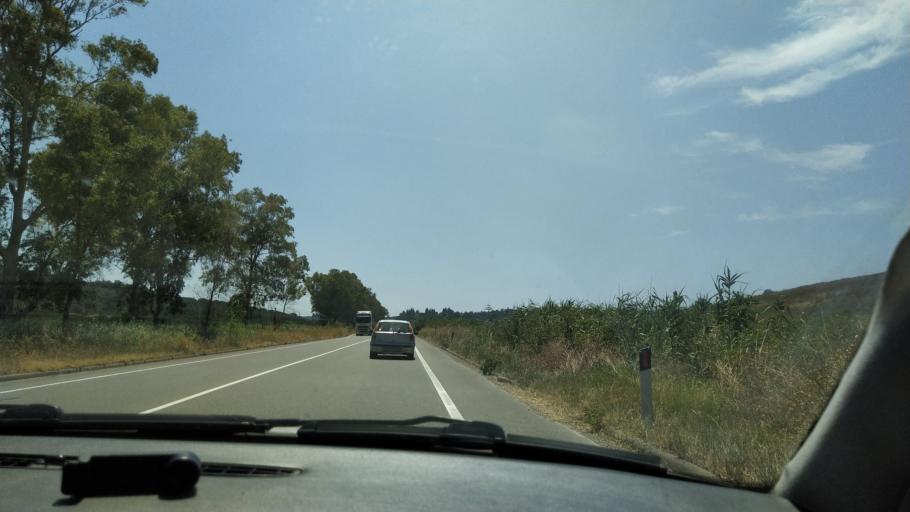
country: IT
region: Apulia
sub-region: Provincia di Taranto
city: Marina di Ginosa
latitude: 40.4398
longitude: 16.7844
